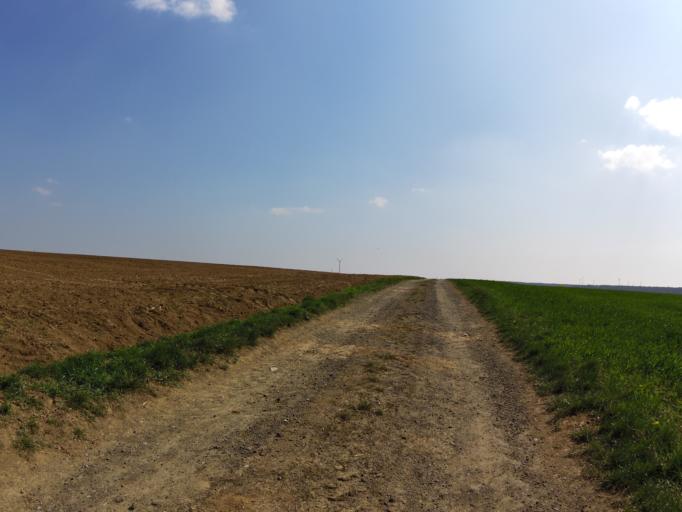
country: DE
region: Bavaria
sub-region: Regierungsbezirk Unterfranken
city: Gerbrunn
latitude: 49.7601
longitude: 10.0113
